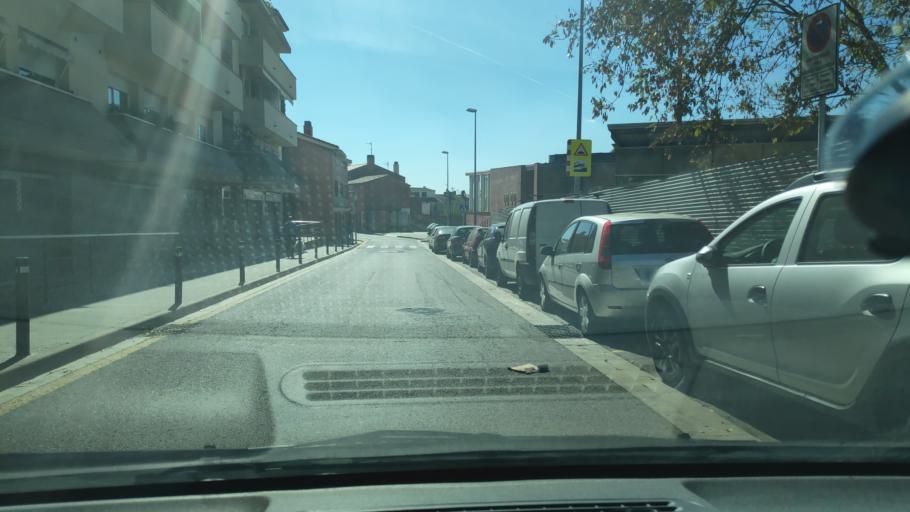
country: ES
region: Catalonia
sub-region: Provincia de Barcelona
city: Rubi
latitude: 41.5033
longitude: 2.0462
